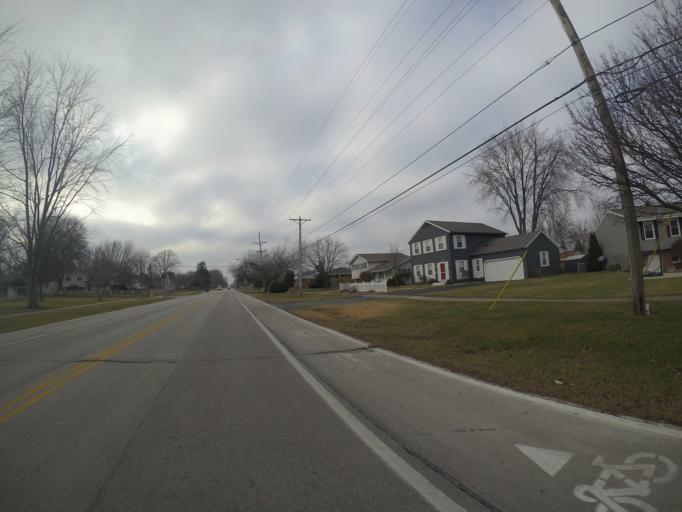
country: US
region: Ohio
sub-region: Lucas County
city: Oregon
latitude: 41.6443
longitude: -83.4714
